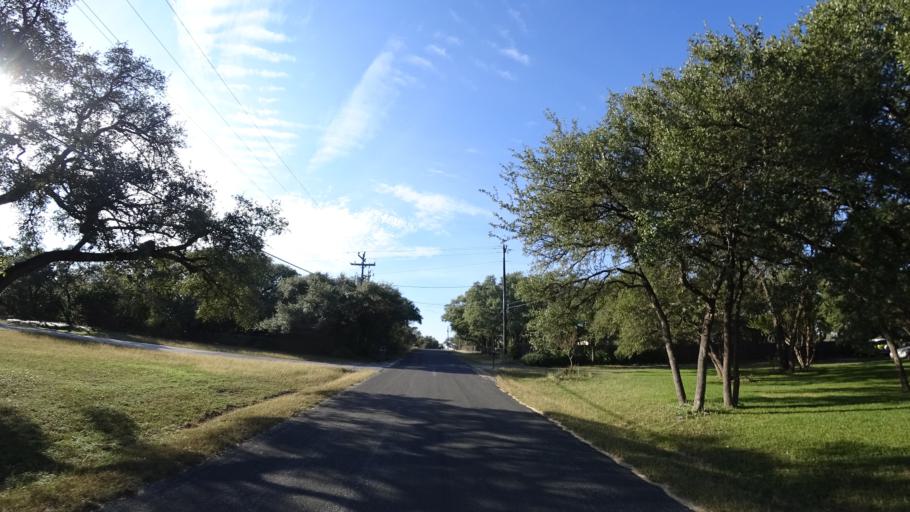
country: US
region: Texas
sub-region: Travis County
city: Barton Creek
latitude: 30.2374
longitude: -97.9115
